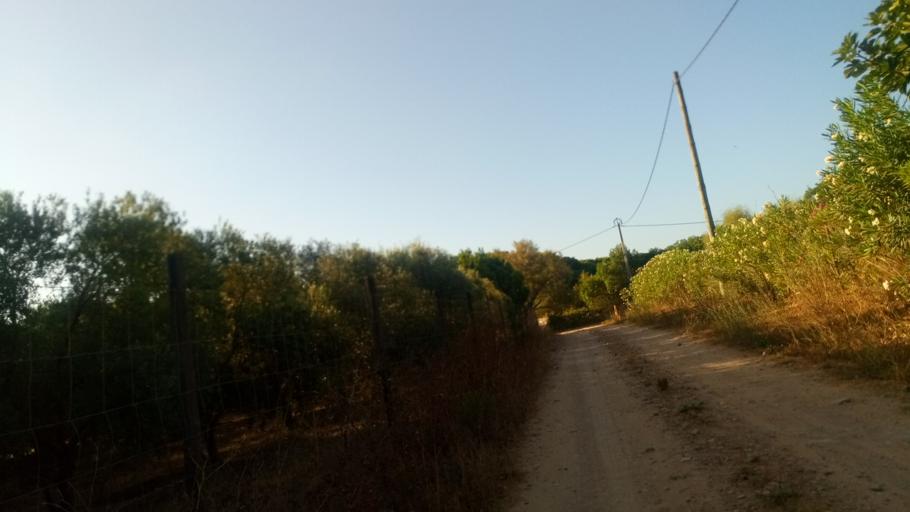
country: PT
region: Faro
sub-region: Tavira
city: Tavira
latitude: 37.1442
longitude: -7.5827
